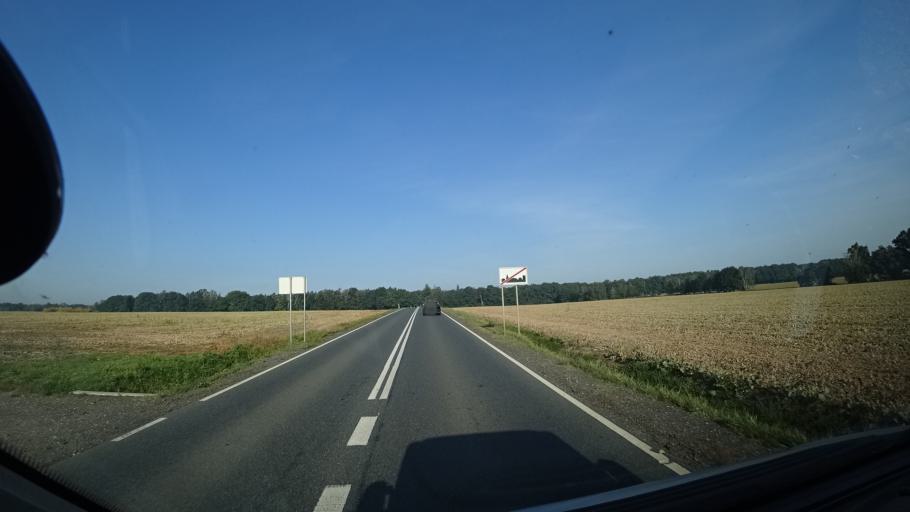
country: PL
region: Silesian Voivodeship
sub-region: Powiat gliwicki
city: Sosnicowice
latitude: 50.2776
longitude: 18.5160
